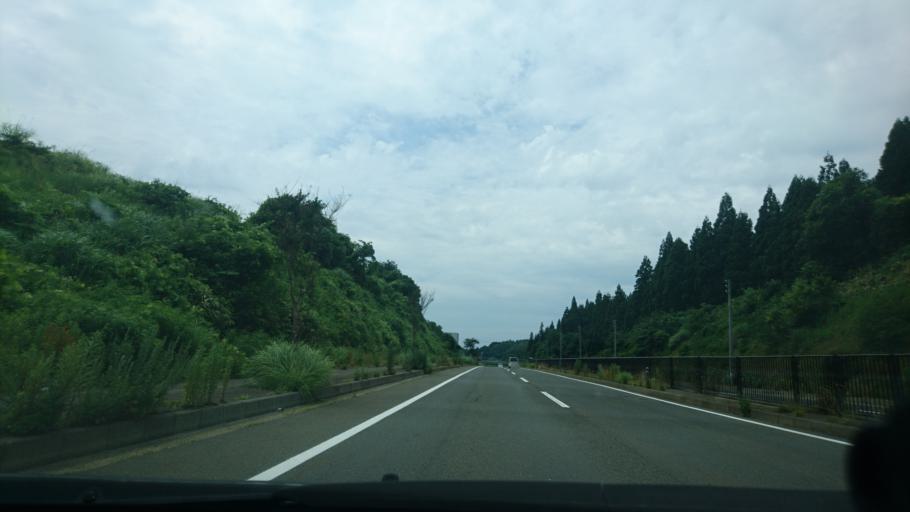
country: JP
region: Akita
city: Akita
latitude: 39.6587
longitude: 140.1976
